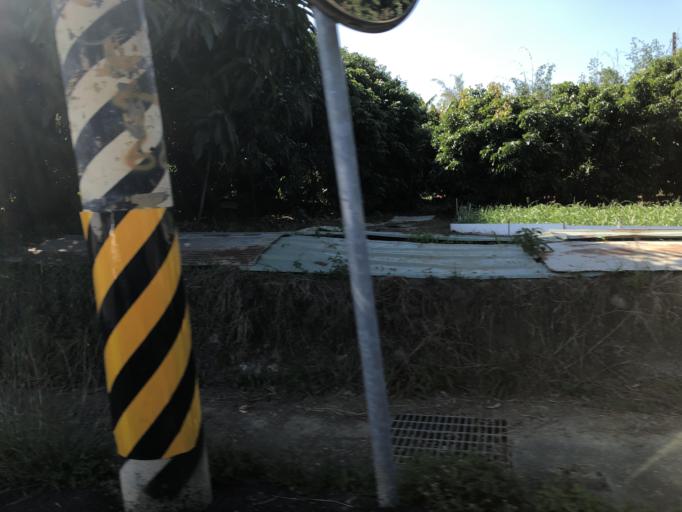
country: TW
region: Taiwan
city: Yujing
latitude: 23.0502
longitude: 120.4018
